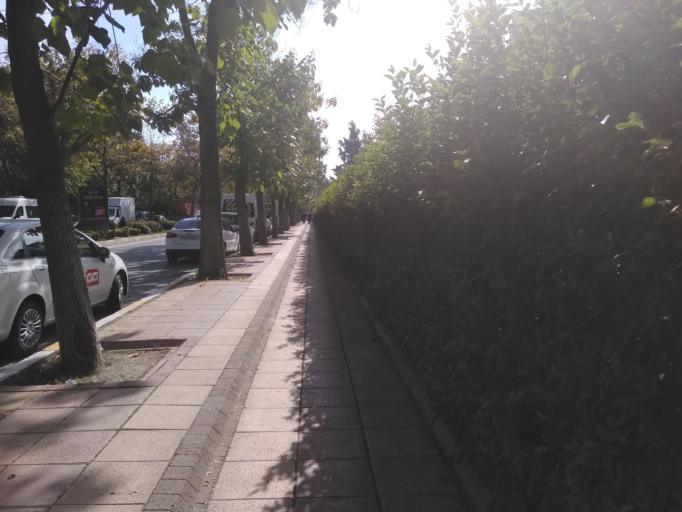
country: TR
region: Istanbul
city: Beylikduezue
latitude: 41.0086
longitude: 28.6432
